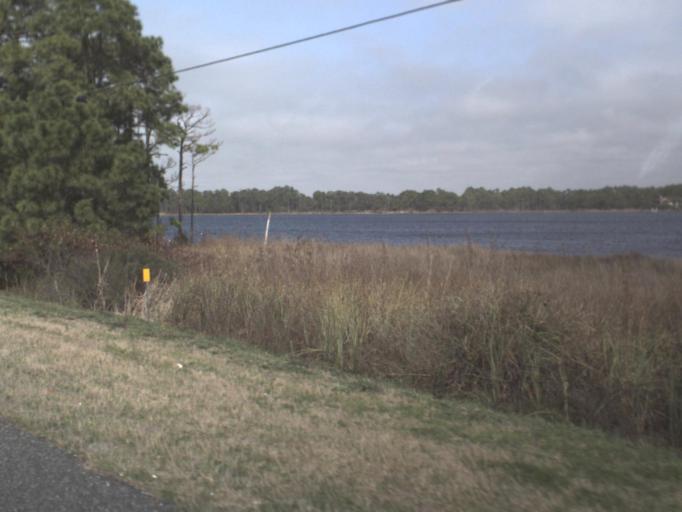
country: US
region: Florida
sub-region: Bay County
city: Laguna Beach
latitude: 30.2689
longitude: -85.9799
